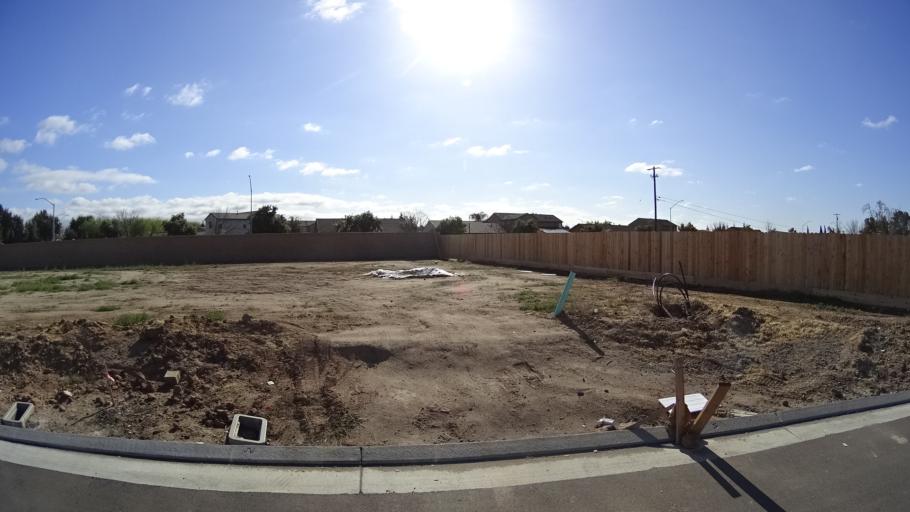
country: US
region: California
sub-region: Fresno County
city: West Park
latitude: 36.8002
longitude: -119.8989
